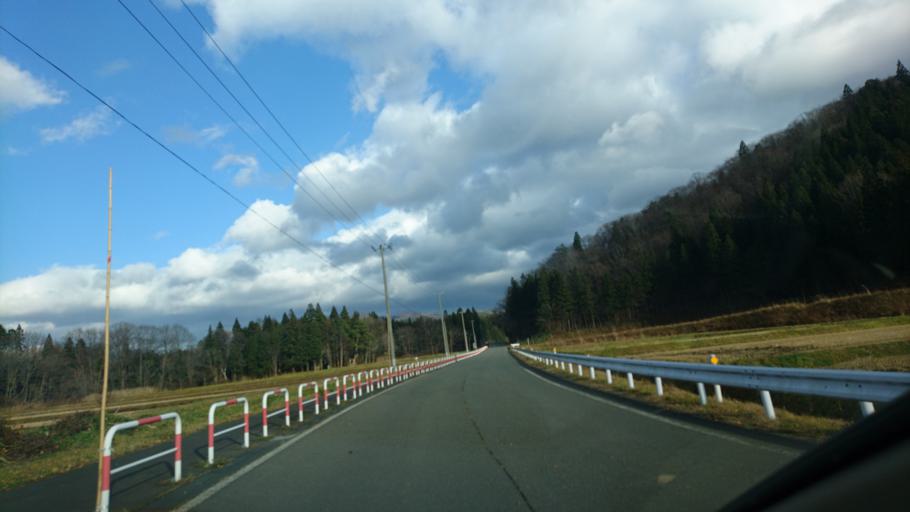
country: JP
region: Akita
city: Kakunodatemachi
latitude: 39.4495
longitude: 140.7781
